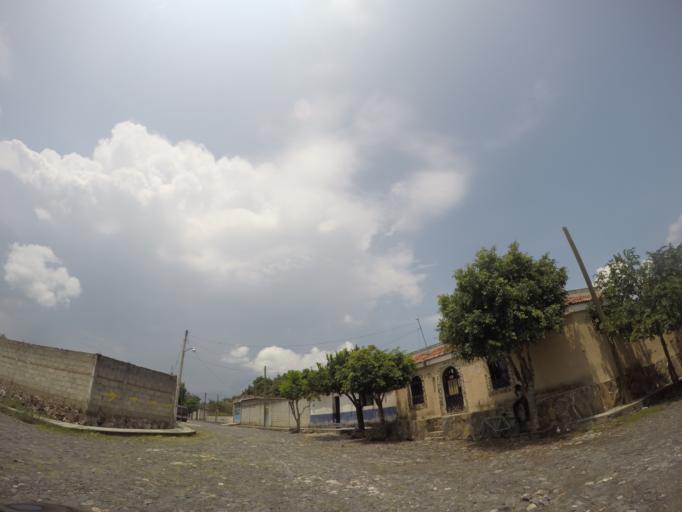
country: MX
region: Nayarit
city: Jala
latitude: 21.1066
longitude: -104.4400
